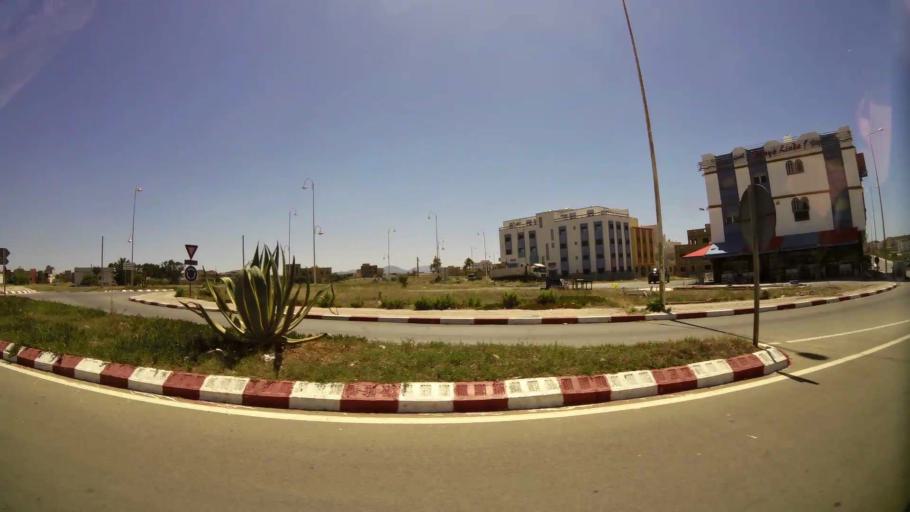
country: MA
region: Oriental
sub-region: Berkane-Taourirt
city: Madagh
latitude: 35.1360
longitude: -2.4128
